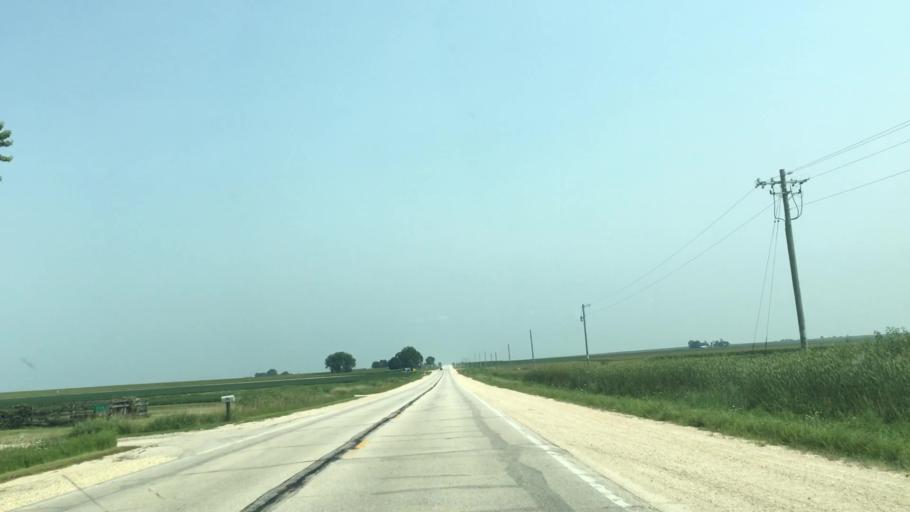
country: US
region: Iowa
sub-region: Fayette County
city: Oelwein
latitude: 42.6873
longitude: -91.8125
